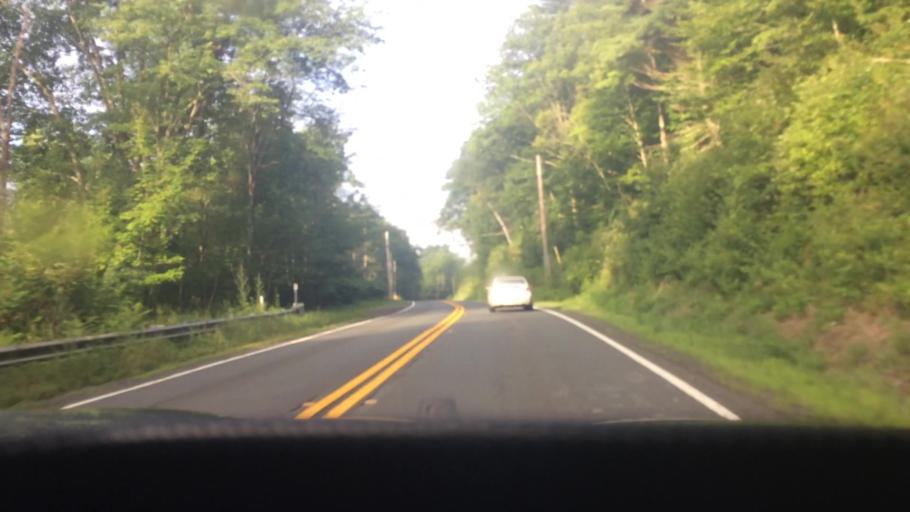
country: US
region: Massachusetts
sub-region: Franklin County
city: Erving
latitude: 42.6033
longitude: -72.4321
